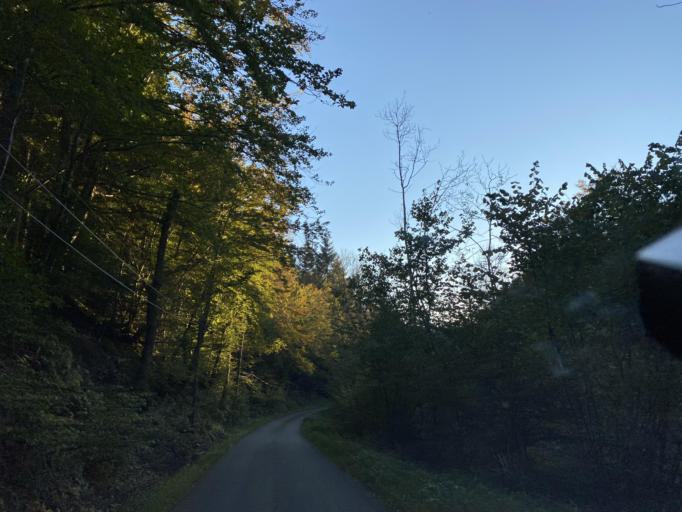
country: FR
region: Rhone-Alpes
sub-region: Departement de la Loire
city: Saint-Just-en-Chevalet
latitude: 45.9521
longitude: 3.8625
